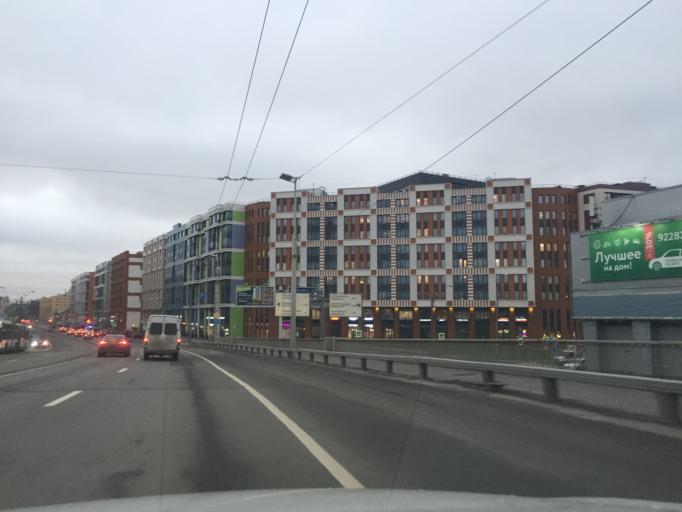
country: RU
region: St.-Petersburg
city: Petrogradka
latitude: 59.9770
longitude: 30.3188
